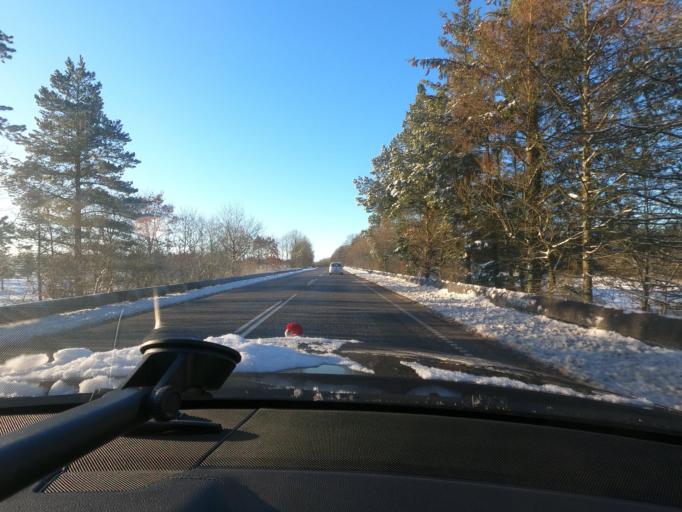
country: DK
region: South Denmark
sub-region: Tonder Kommune
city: Sherrebek
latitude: 55.1718
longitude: 8.7750
